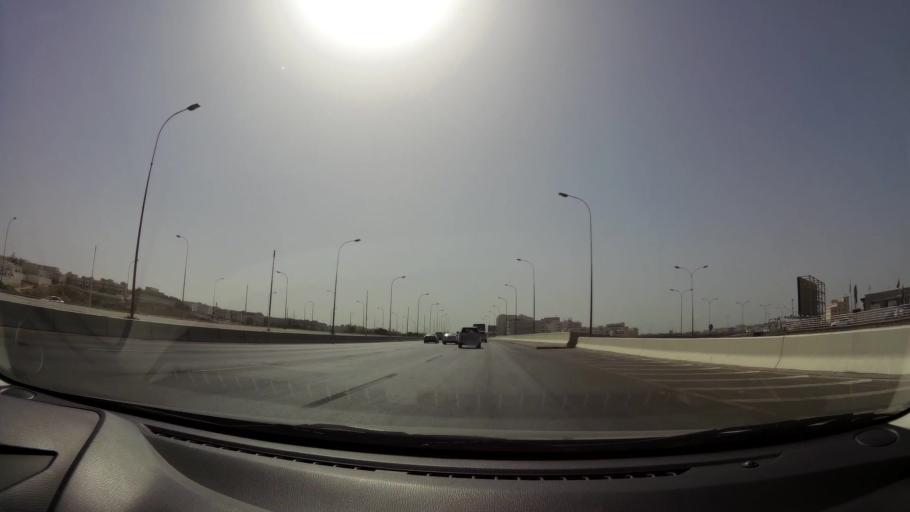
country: OM
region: Muhafazat Masqat
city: Muscat
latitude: 23.6087
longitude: 58.5001
